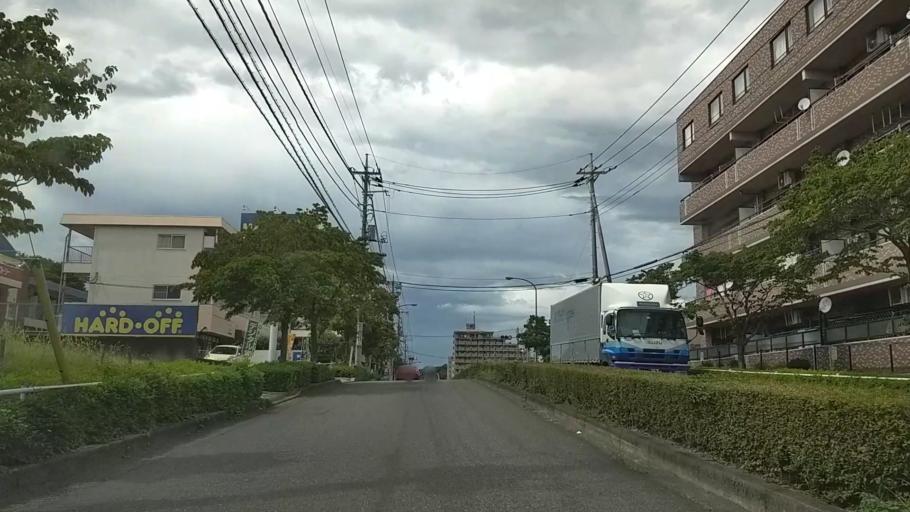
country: JP
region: Tokyo
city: Hachioji
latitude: 35.6392
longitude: 139.3089
